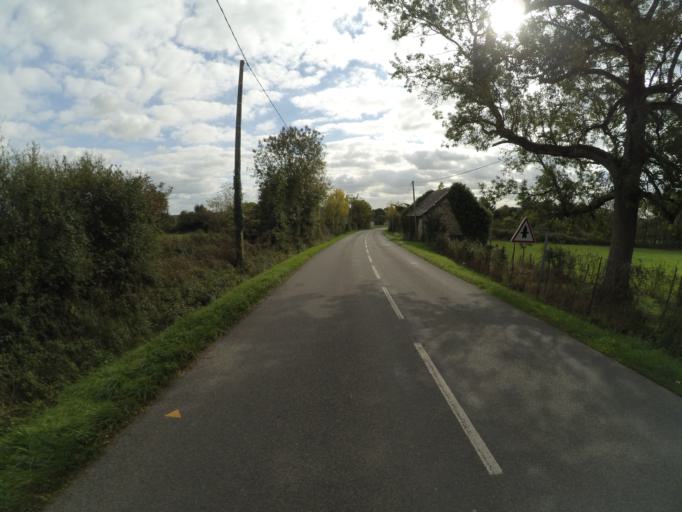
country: FR
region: Pays de la Loire
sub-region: Departement de la Loire-Atlantique
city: Bouvron
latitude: 47.4776
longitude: -1.8397
